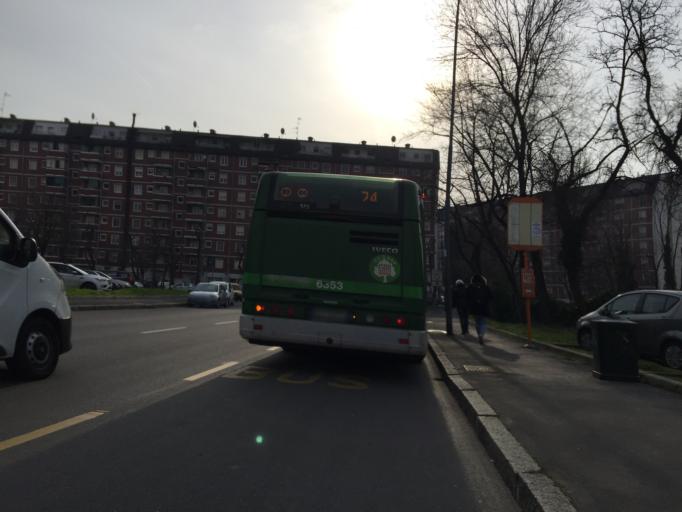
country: IT
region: Lombardy
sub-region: Citta metropolitana di Milano
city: Romano Banco
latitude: 45.4300
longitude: 9.1497
